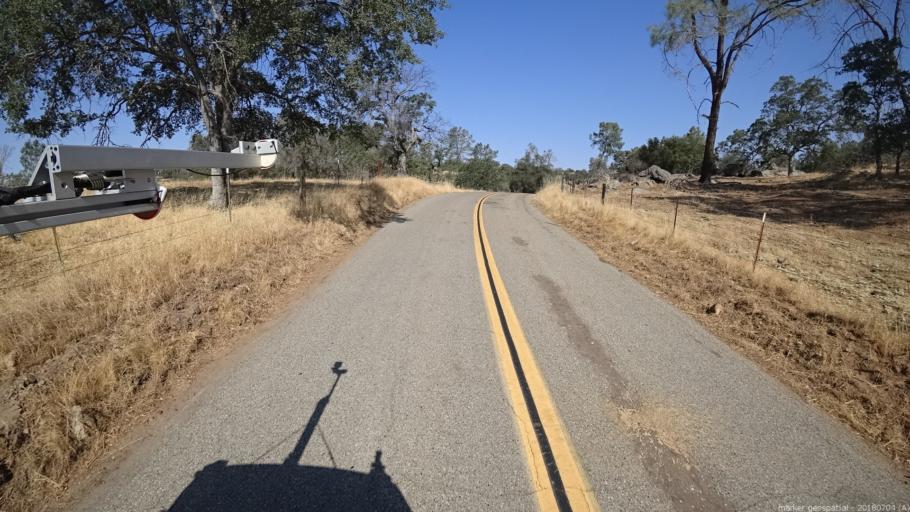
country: US
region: California
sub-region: Madera County
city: Yosemite Lakes
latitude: 37.1106
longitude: -119.6699
